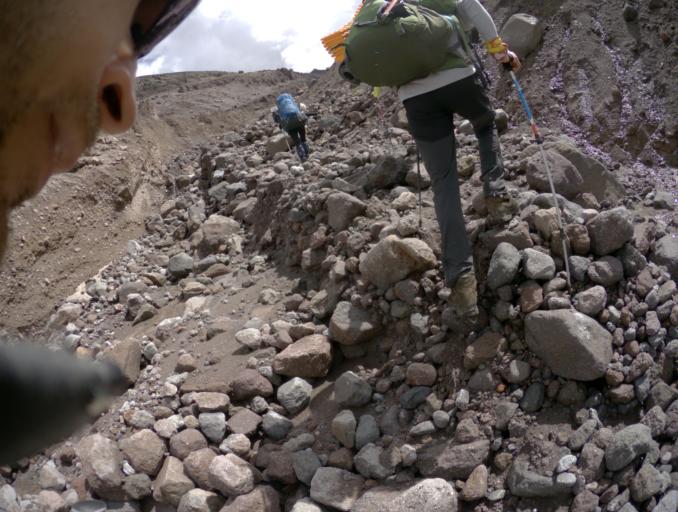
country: RU
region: Kabardino-Balkariya
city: Terskol
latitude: 43.3835
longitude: 42.3691
